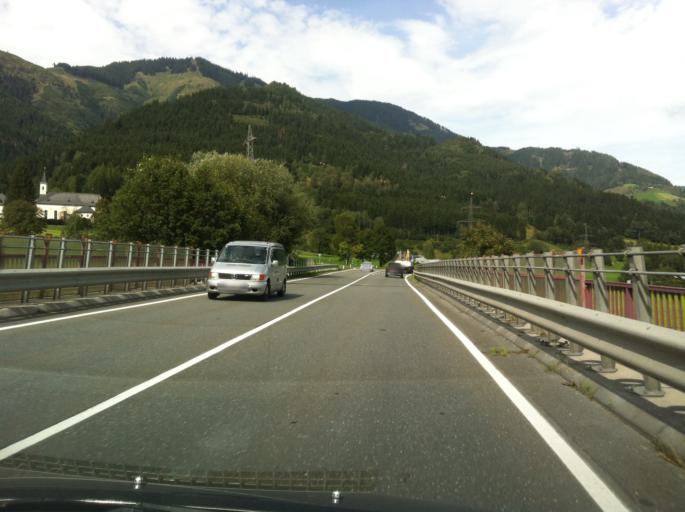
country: AT
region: Salzburg
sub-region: Politischer Bezirk Zell am See
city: Bruck an der Grossglocknerstrasse
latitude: 47.2832
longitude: 12.8449
